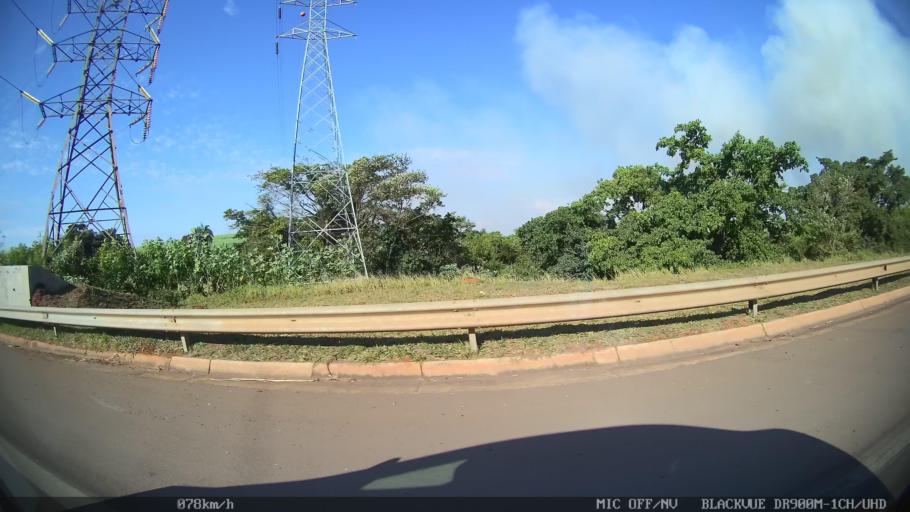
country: BR
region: Sao Paulo
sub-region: Piracicaba
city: Piracicaba
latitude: -22.6909
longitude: -47.5996
